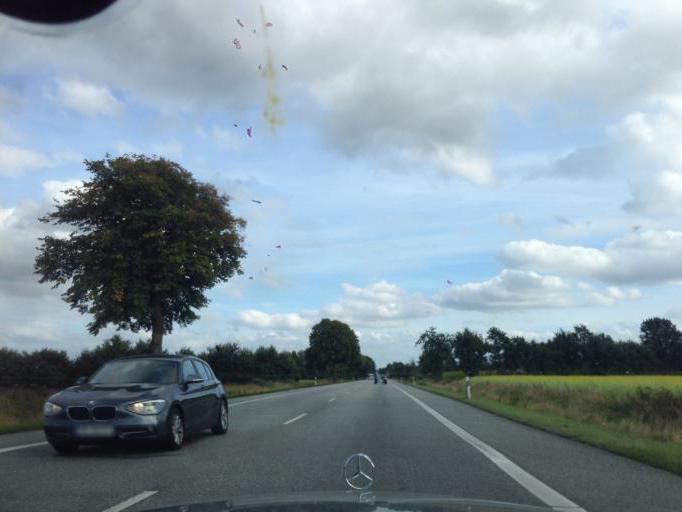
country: DE
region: Schleswig-Holstein
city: Wahlstedt
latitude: 53.9765
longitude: 10.2169
